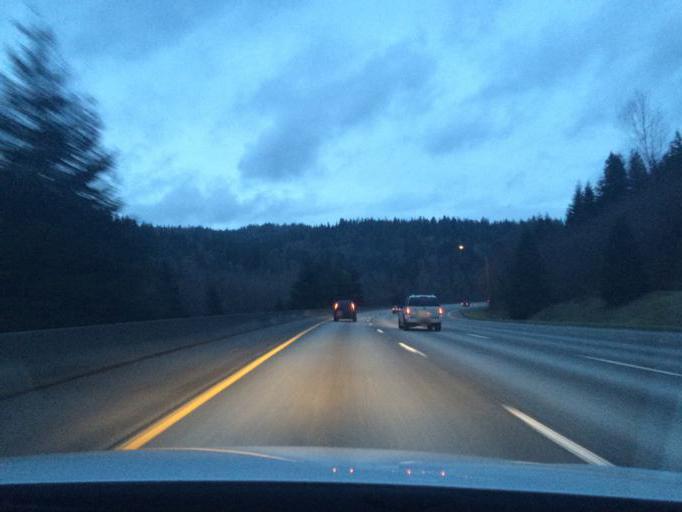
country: US
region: Washington
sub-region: King County
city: Issaquah
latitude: 47.5339
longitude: -121.9755
